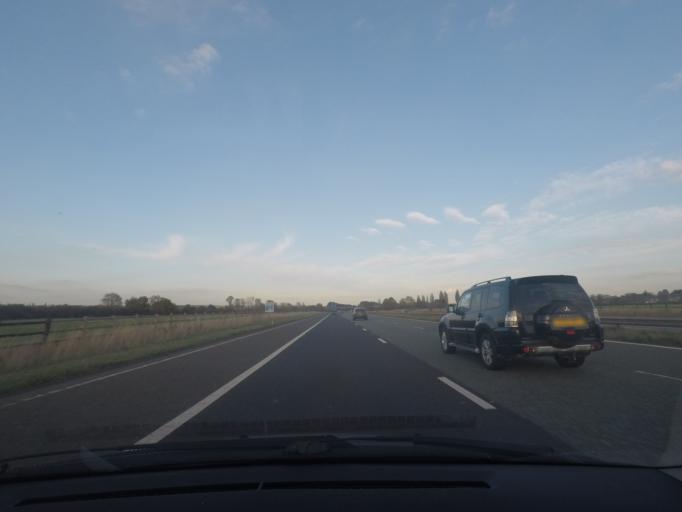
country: GB
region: England
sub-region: North Lincolnshire
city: Brigg
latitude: 53.5680
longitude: -0.4775
